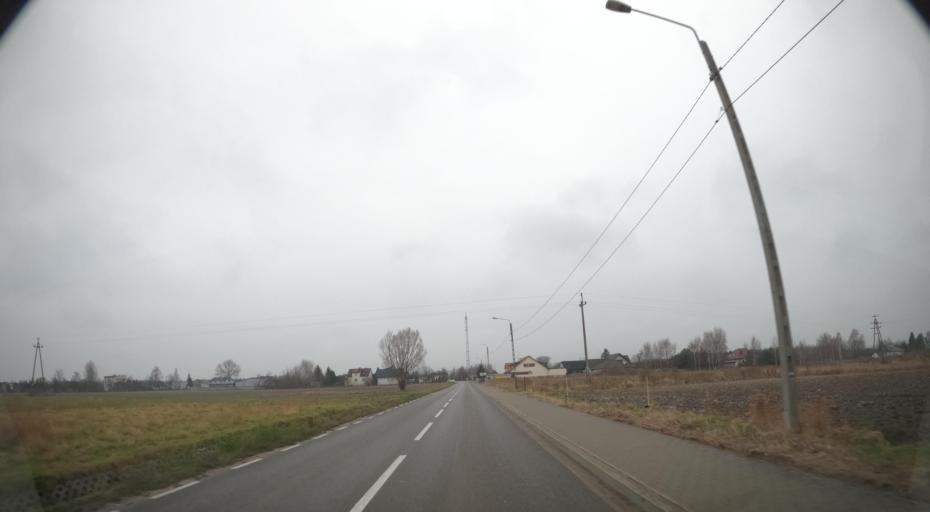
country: PL
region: Masovian Voivodeship
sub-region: Powiat radomski
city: Skaryszew
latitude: 51.3798
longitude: 21.2532
